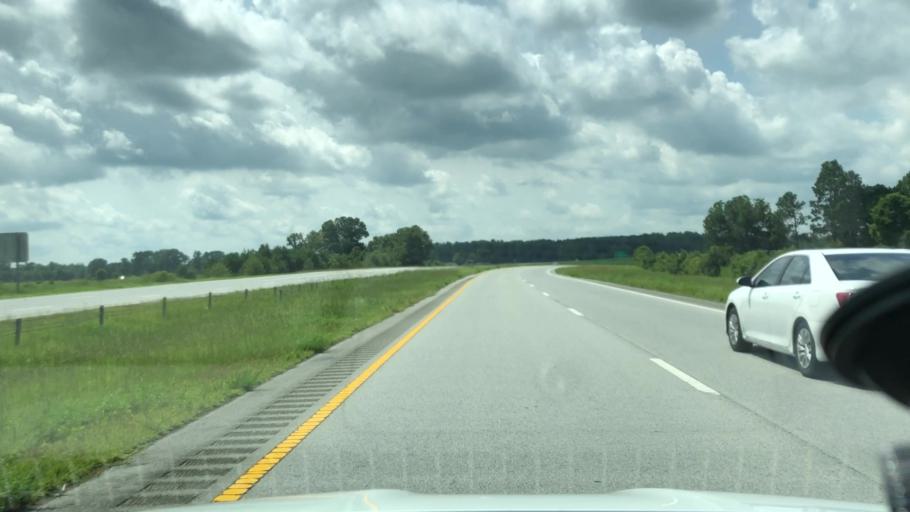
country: US
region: North Carolina
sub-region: Beaufort County
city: Washington
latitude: 35.5125
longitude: -77.0867
